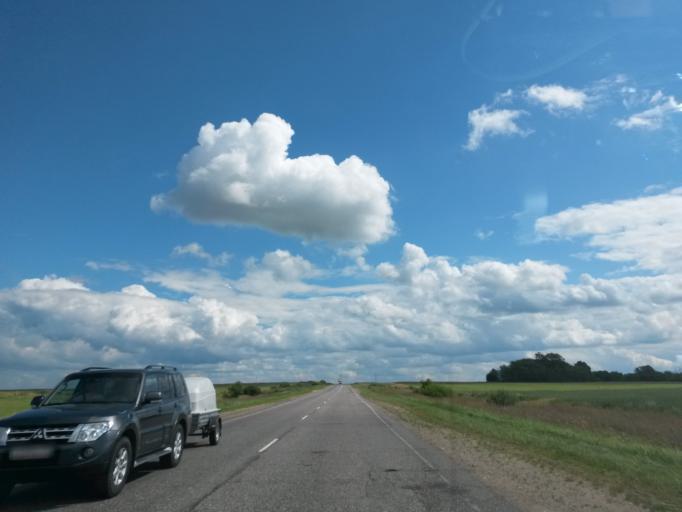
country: RU
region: Ivanovo
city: Pistsovo
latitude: 57.1819
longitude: 40.4777
